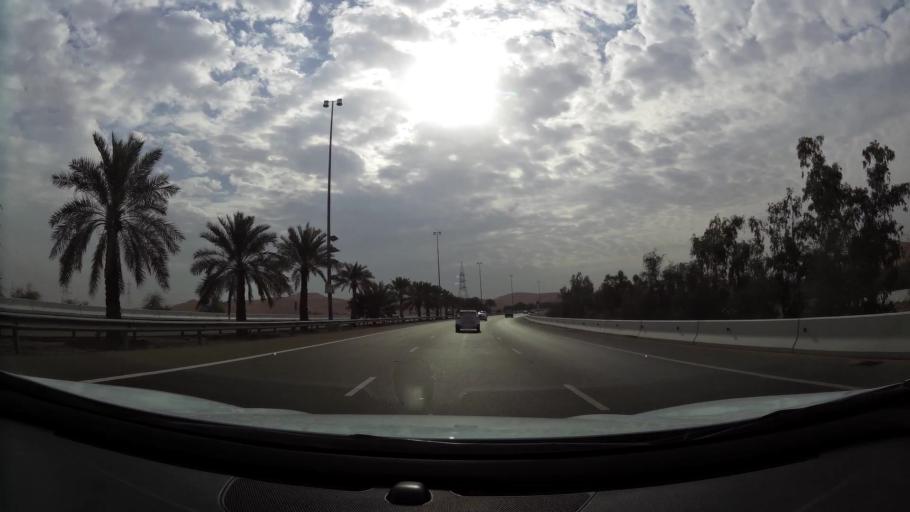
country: AE
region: Abu Dhabi
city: Al Ain
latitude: 24.2238
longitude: 55.5638
